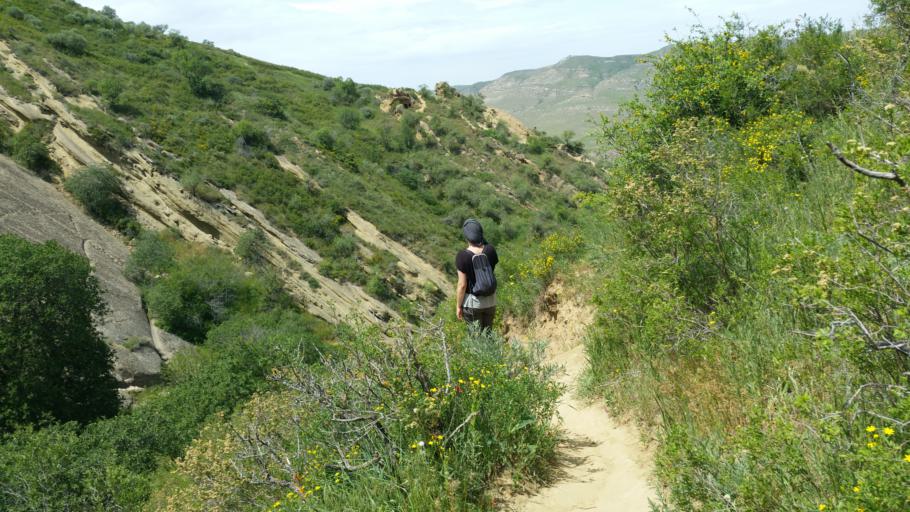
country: AZ
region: Agstafa
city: Saloglu
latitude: 41.4460
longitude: 45.3762
